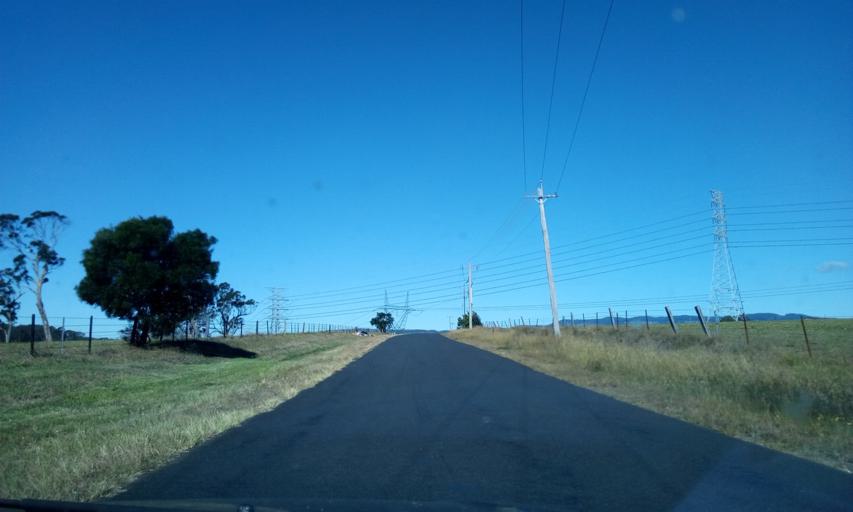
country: AU
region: New South Wales
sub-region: Wollongong
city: Dapto
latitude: -34.5219
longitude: 150.7790
